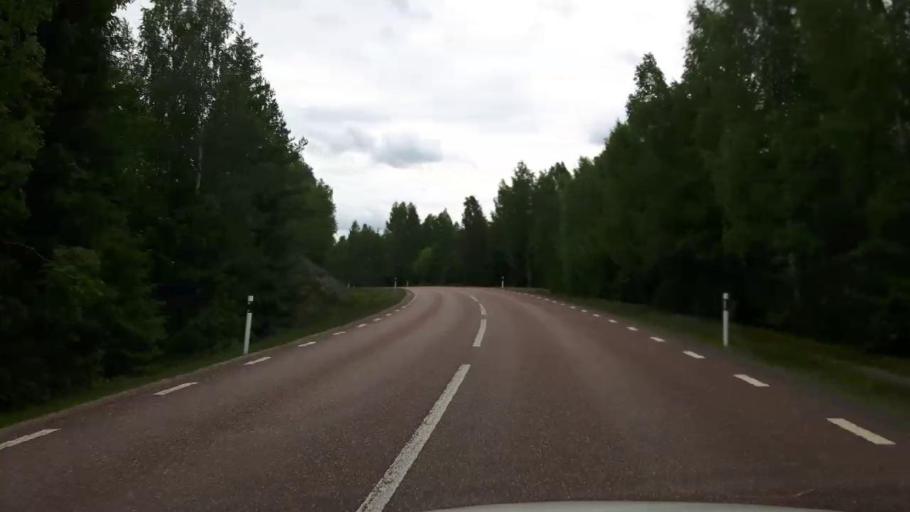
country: SE
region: Dalarna
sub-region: Hedemora Kommun
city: Brunna
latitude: 60.1879
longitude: 15.9990
